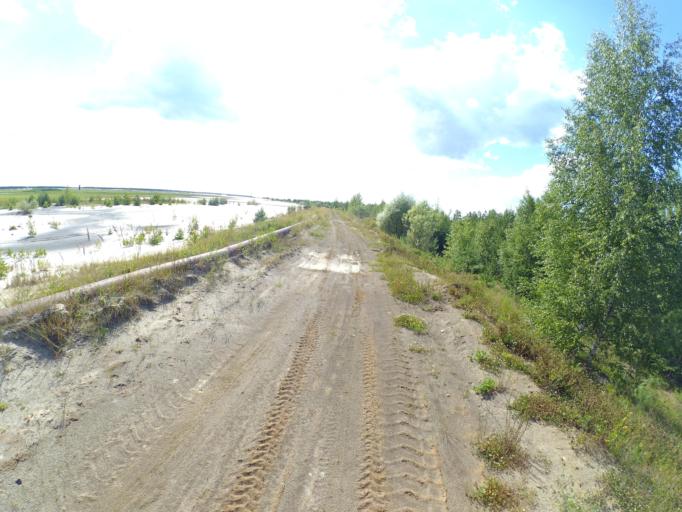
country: RU
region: Moskovskaya
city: Fosforitnyy
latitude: 55.3286
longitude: 38.9233
